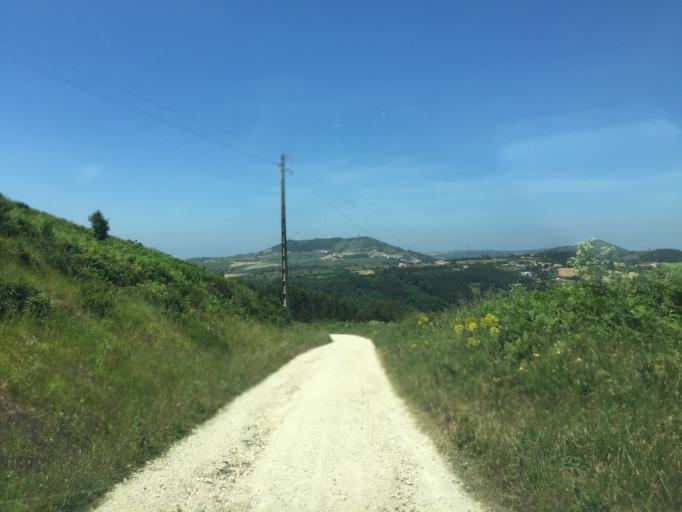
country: PT
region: Lisbon
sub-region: Mafra
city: Venda do Pinheiro
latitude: 38.8978
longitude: -9.2383
